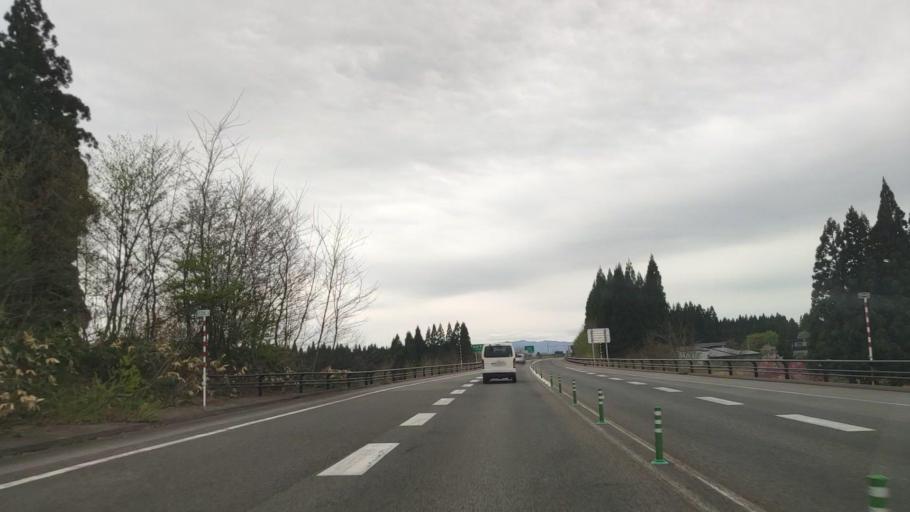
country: JP
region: Akita
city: Odate
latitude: 40.3095
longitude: 140.5758
